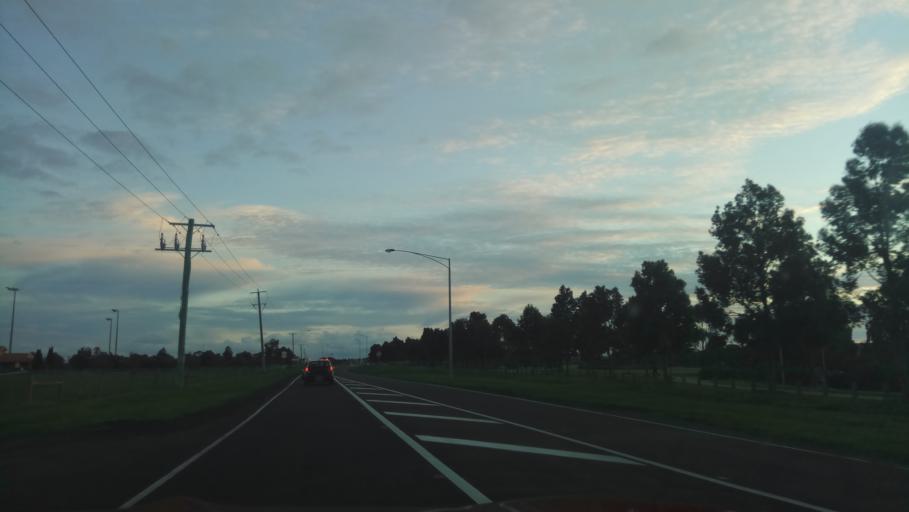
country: AU
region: Victoria
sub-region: Wyndham
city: Point Cook
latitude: -37.9062
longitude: 144.7525
